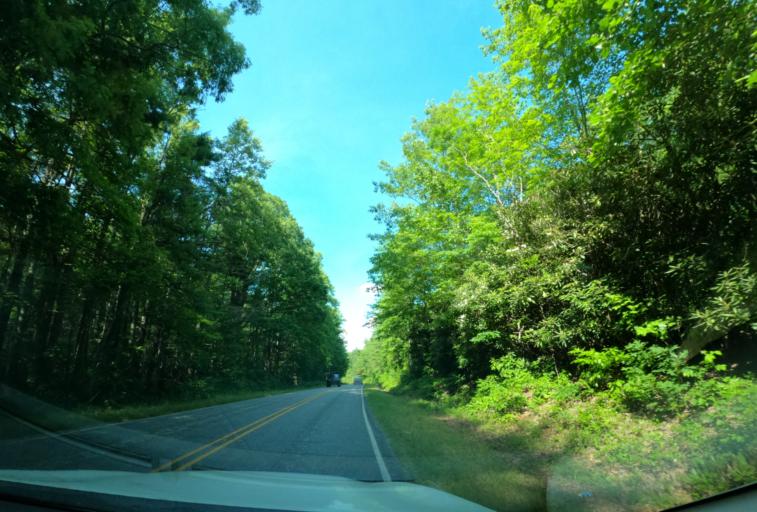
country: US
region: North Carolina
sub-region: Transylvania County
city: Brevard
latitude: 35.1848
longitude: -82.6400
